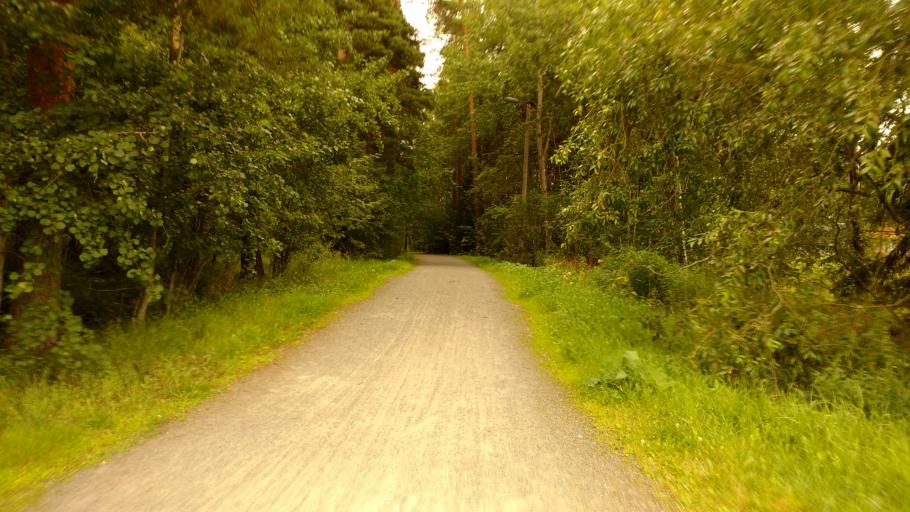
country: FI
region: Varsinais-Suomi
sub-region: Turku
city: Kaarina
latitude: 60.4390
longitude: 22.3281
